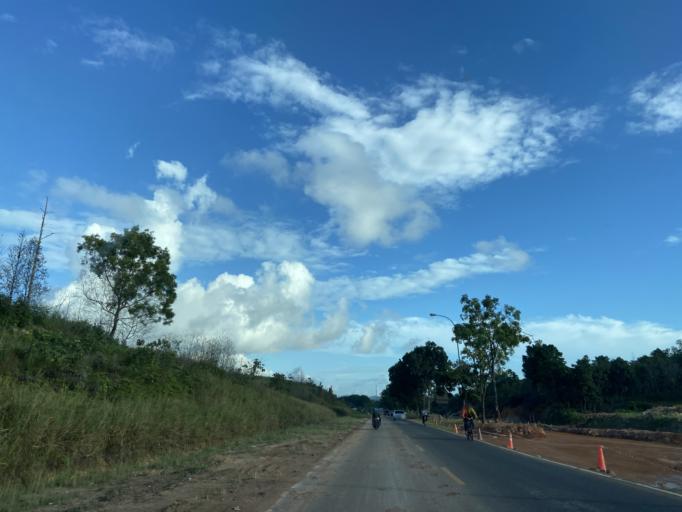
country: SG
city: Singapore
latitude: 1.0202
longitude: 104.0138
